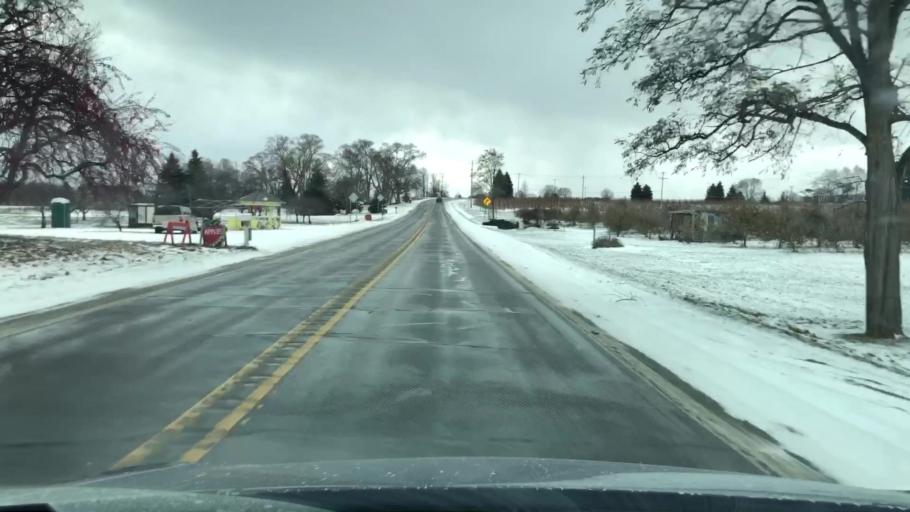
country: US
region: Michigan
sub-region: Antrim County
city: Elk Rapids
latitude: 44.8682
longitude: -85.5157
